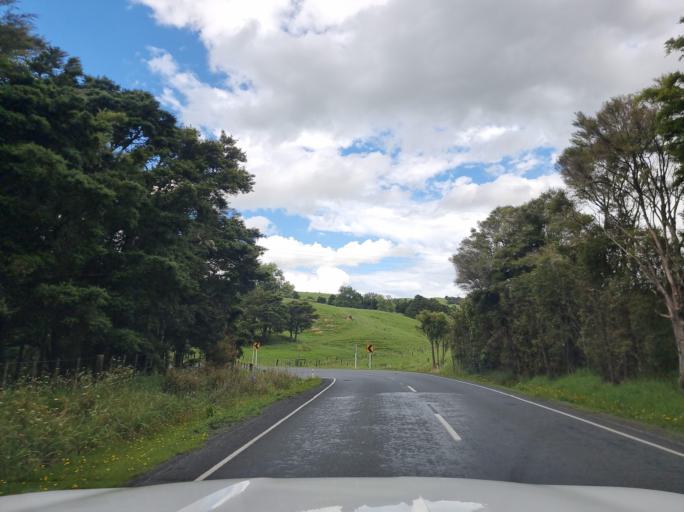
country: NZ
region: Northland
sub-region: Whangarei
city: Maungatapere
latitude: -35.8619
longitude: 174.2503
